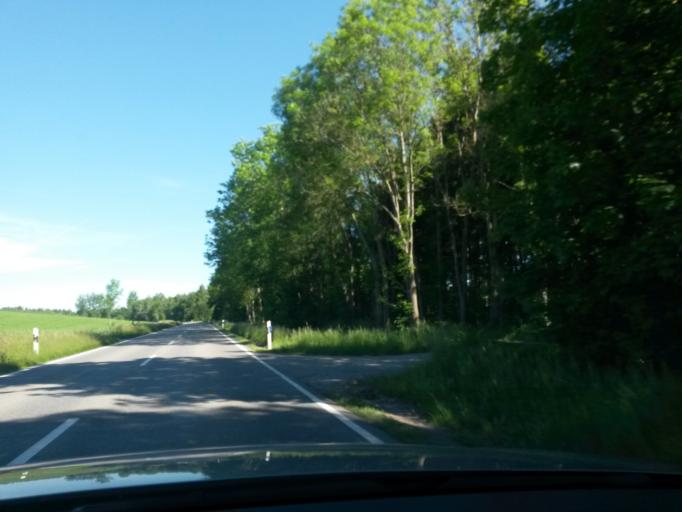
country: DE
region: Baden-Wuerttemberg
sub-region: Tuebingen Region
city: Bad Buchau
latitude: 48.0415
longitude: 9.6314
